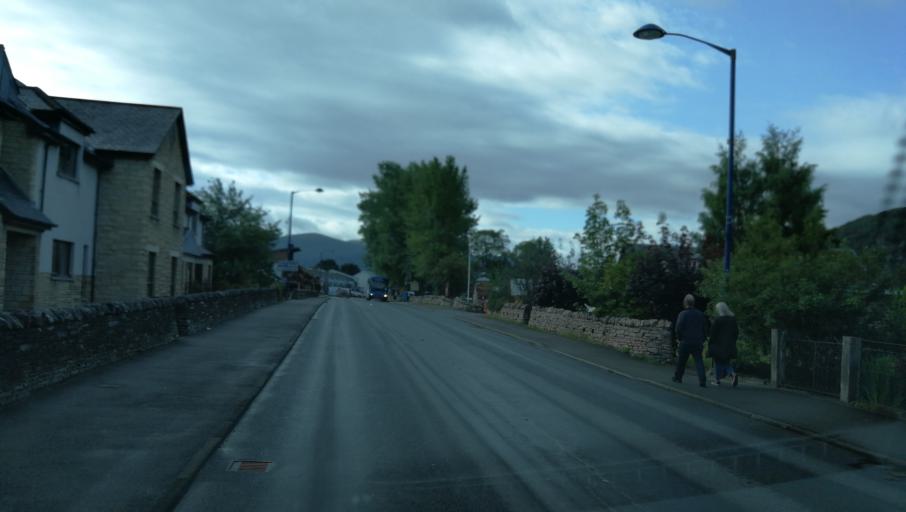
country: GB
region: Scotland
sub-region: Highland
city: Aviemore
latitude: 57.1941
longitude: -3.8290
